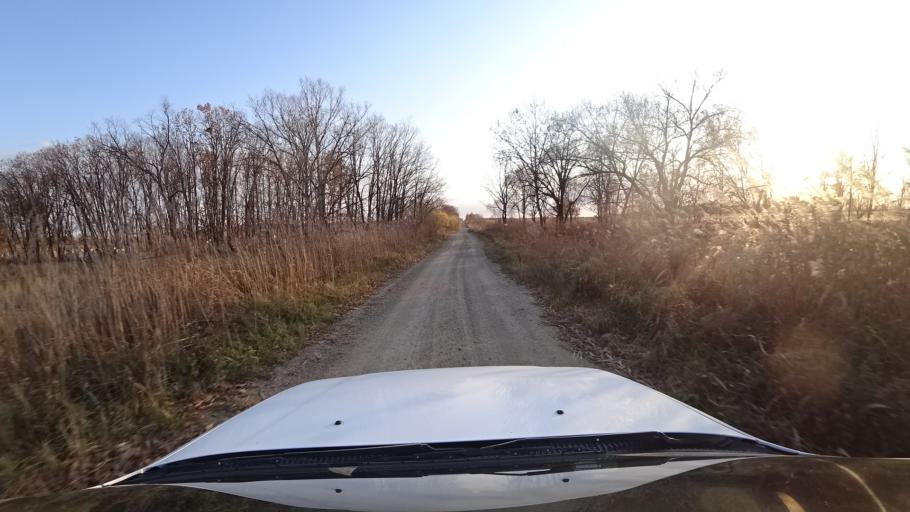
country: RU
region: Primorskiy
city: Lazo
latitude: 45.8156
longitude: 133.6110
